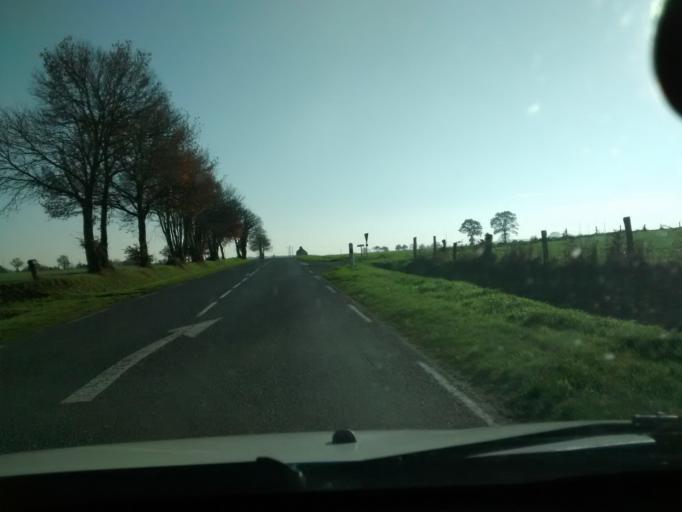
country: FR
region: Brittany
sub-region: Departement d'Ille-et-Vilaine
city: Antrain
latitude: 48.5076
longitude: -1.4761
